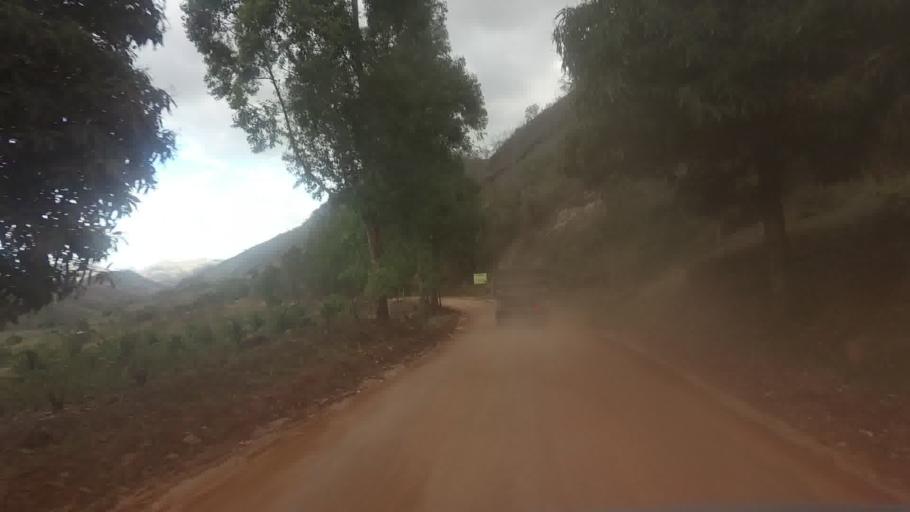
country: BR
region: Espirito Santo
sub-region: Mimoso Do Sul
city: Mimoso do Sul
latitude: -20.9472
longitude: -41.3930
